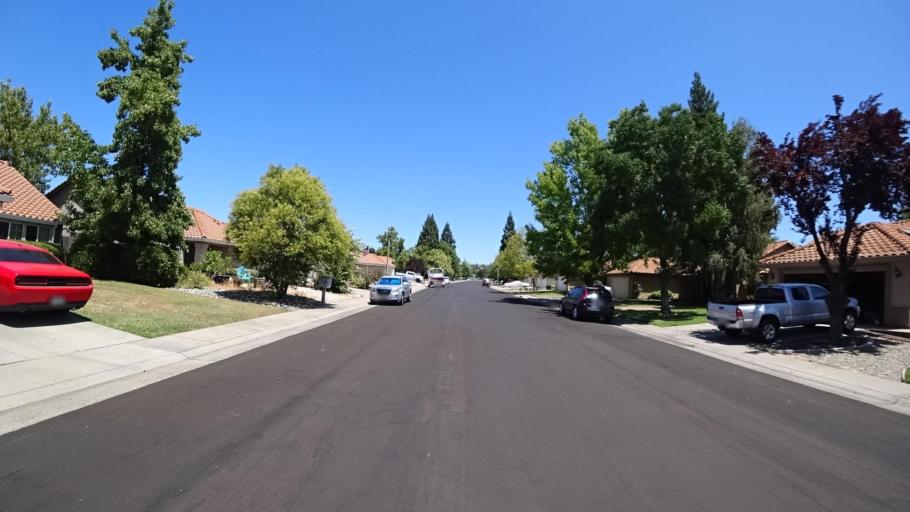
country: US
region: California
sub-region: Placer County
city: Rocklin
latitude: 38.8223
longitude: -121.2594
